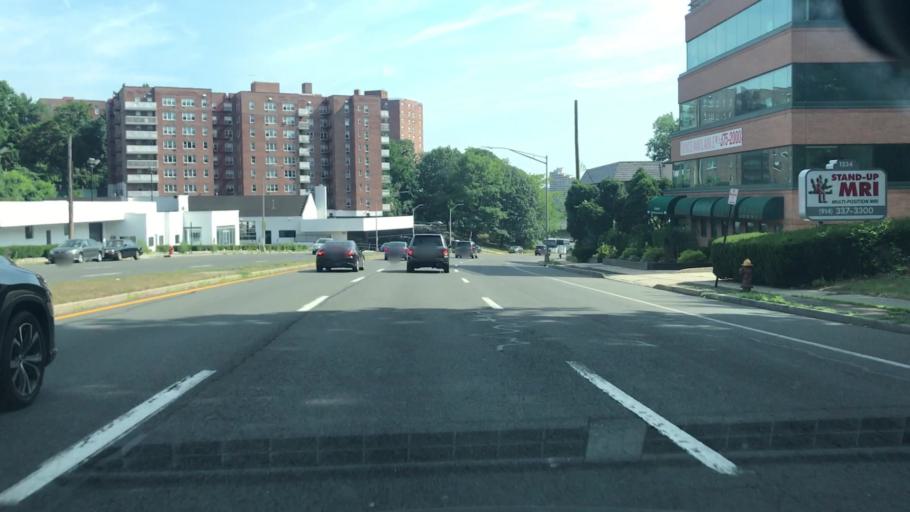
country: US
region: New York
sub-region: Westchester County
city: Bronxville
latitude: 40.9430
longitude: -73.8519
